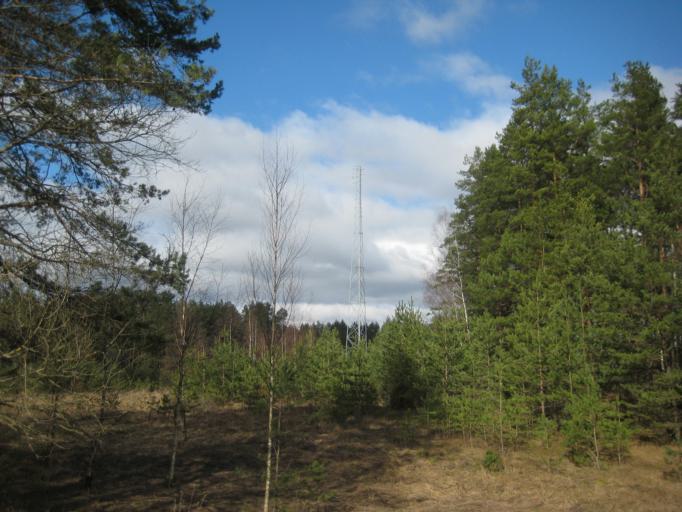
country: LT
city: Zarasai
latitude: 55.6907
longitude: 26.1377
